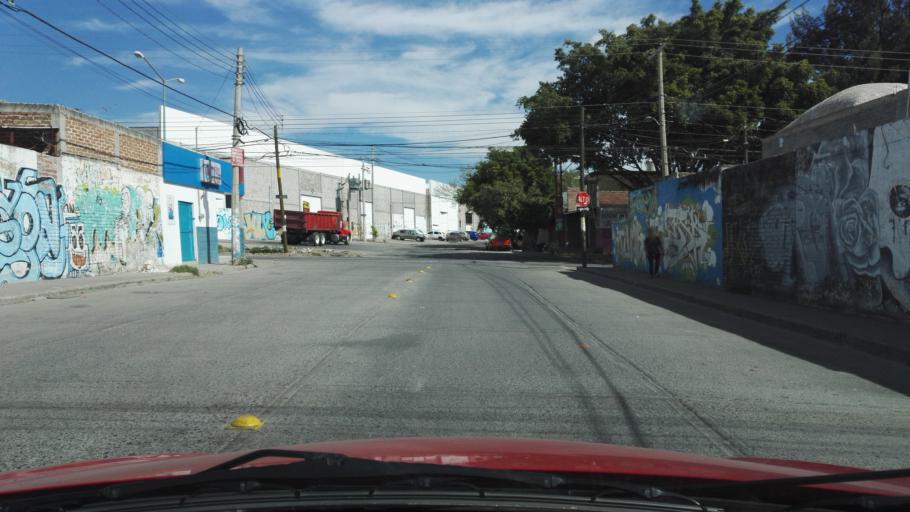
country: MX
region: Guanajuato
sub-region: Leon
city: Medina
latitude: 21.1116
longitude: -101.6318
